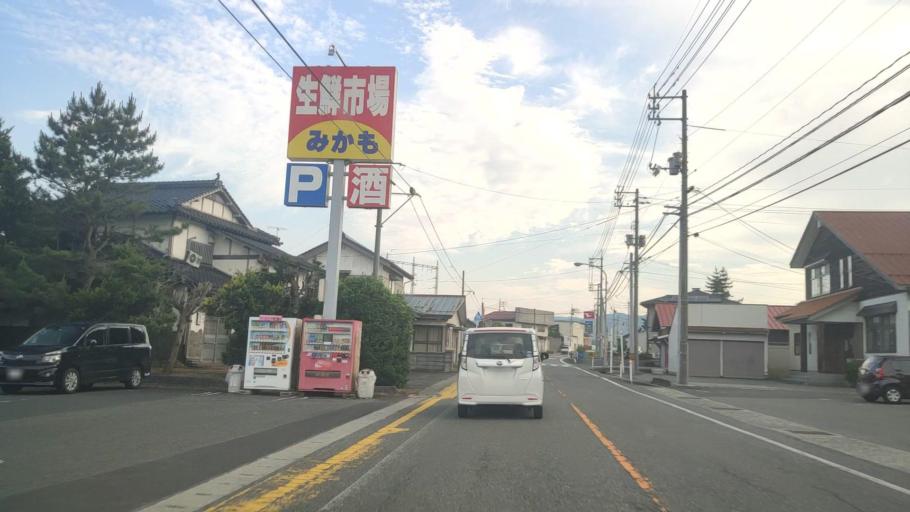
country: JP
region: Tottori
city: Kurayoshi
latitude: 35.2835
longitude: 133.6958
